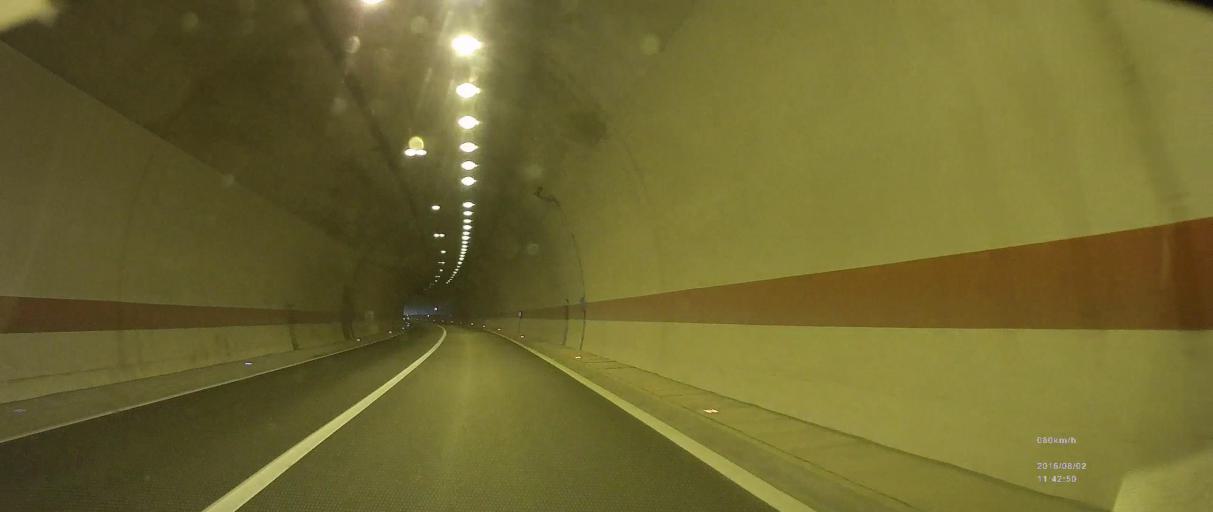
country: HR
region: Dubrovacko-Neretvanska
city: Komin
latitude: 43.0542
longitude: 17.4810
